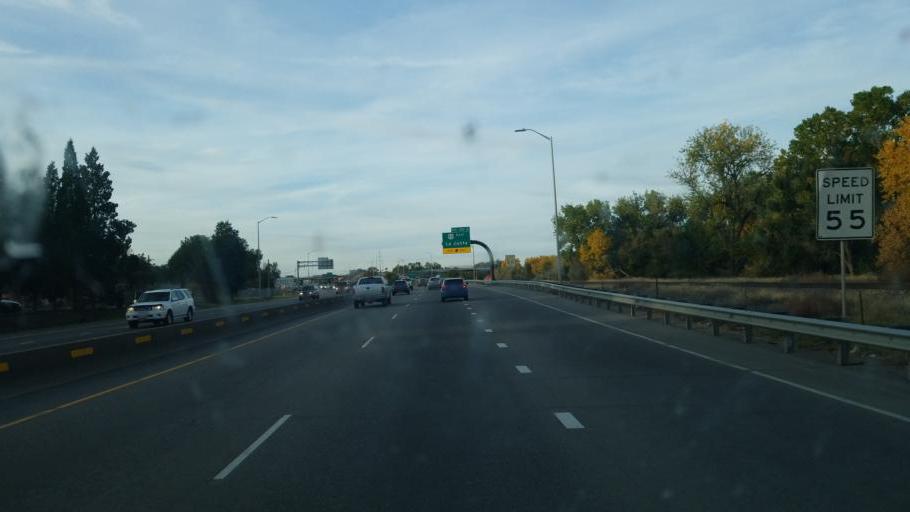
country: US
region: Colorado
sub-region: Pueblo County
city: Pueblo
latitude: 38.2834
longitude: -104.6051
